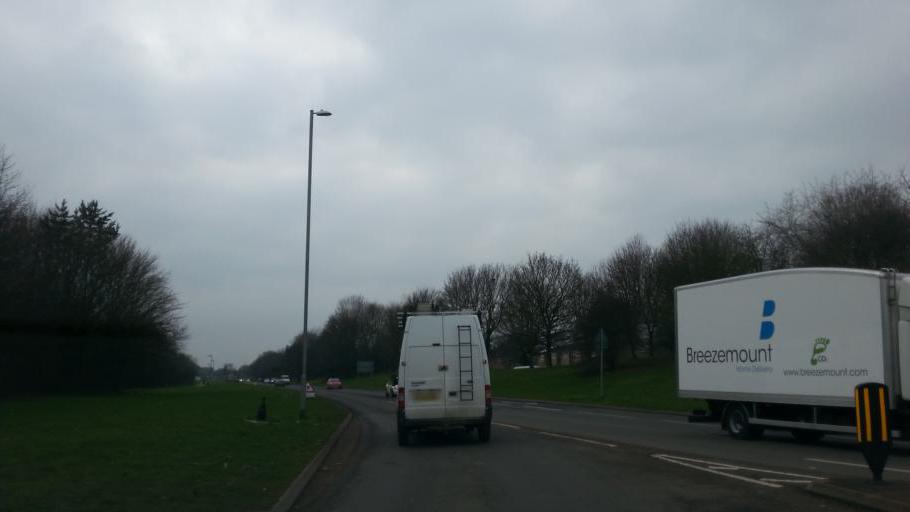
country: GB
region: England
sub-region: Northamptonshire
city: Corby
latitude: 52.4773
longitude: -0.7109
